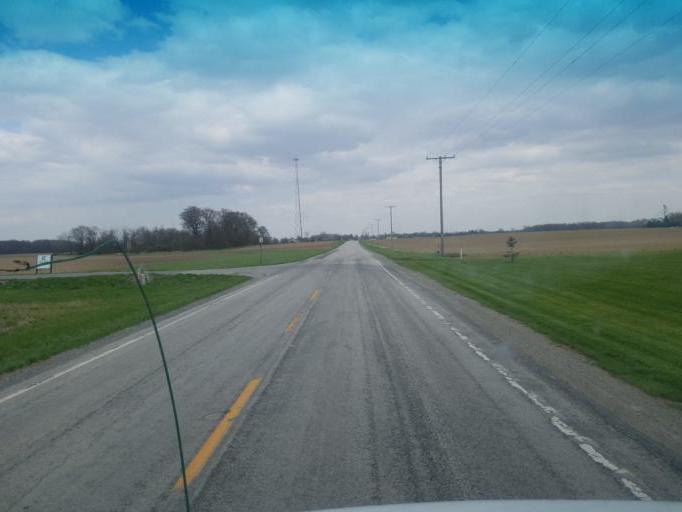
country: US
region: Ohio
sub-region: Wyandot County
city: Upper Sandusky
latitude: 40.9496
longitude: -83.1946
